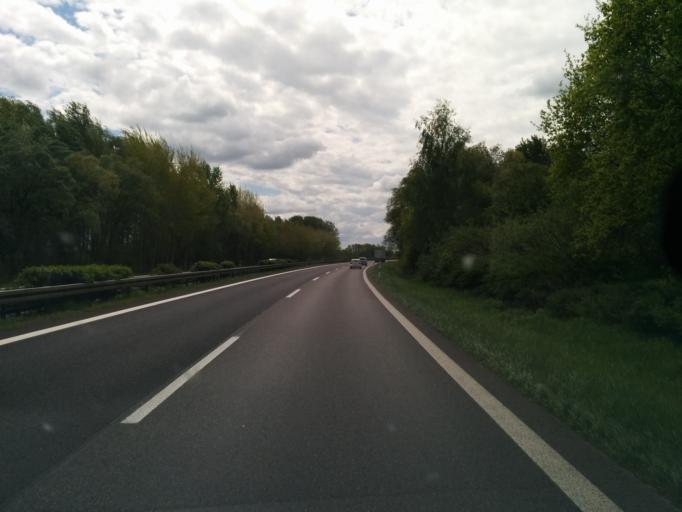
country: DE
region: Brandenburg
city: Wustermark
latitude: 52.4836
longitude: 12.9634
